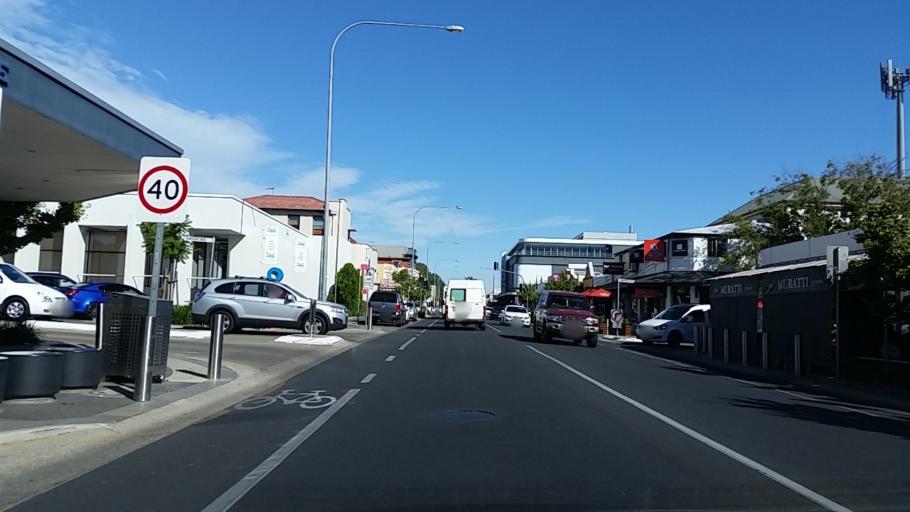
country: AU
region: South Australia
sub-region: Prospect
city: Prospect
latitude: -34.8870
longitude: 138.5940
